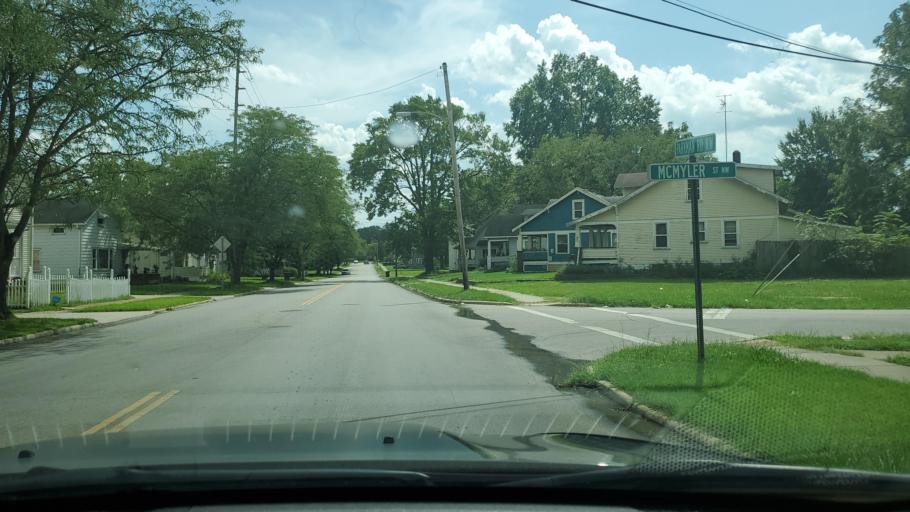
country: US
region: Ohio
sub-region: Trumbull County
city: Warren
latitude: 41.2398
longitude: -80.8350
